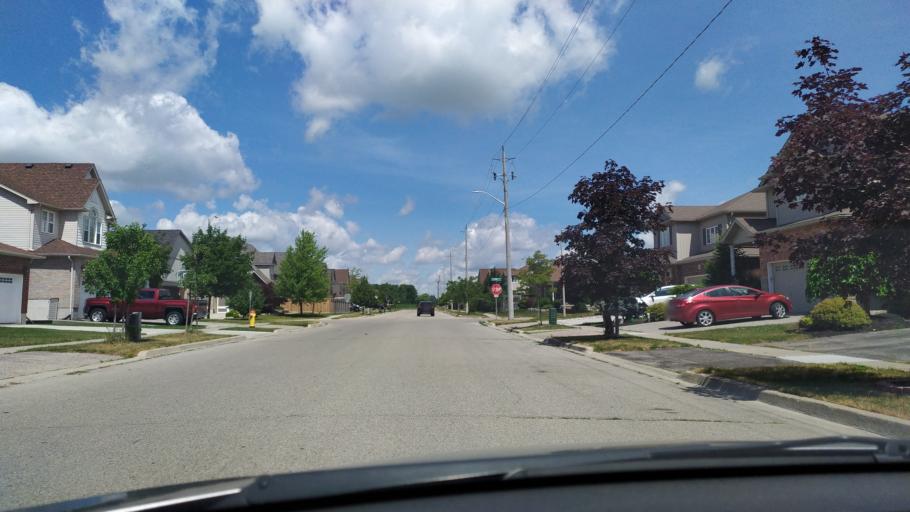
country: CA
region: Ontario
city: Kitchener
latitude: 43.4094
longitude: -80.6717
